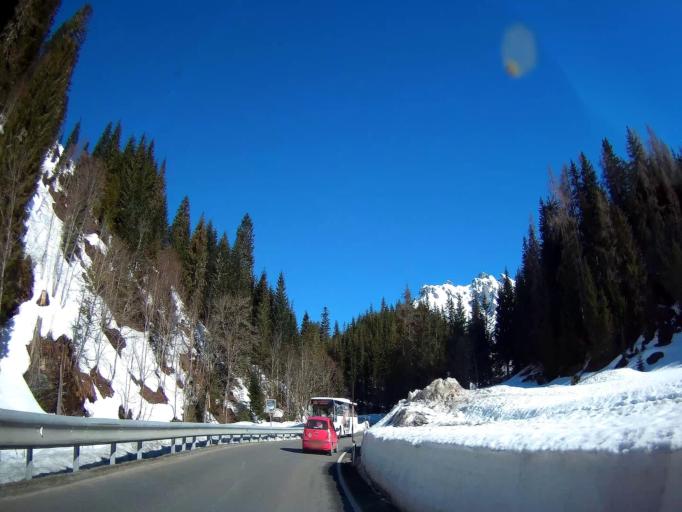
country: AT
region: Salzburg
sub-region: Politischer Bezirk Zell am See
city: Dienten am Hochkonig
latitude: 47.3940
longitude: 13.0147
